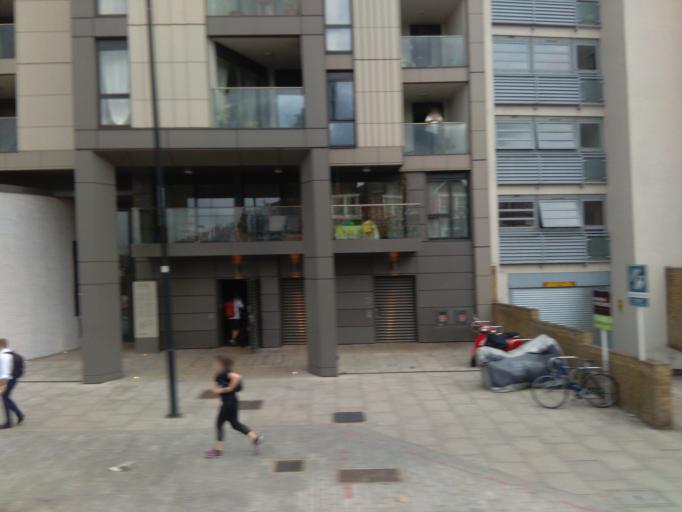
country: GB
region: England
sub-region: Greater London
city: Battersea
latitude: 51.4521
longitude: -0.1479
